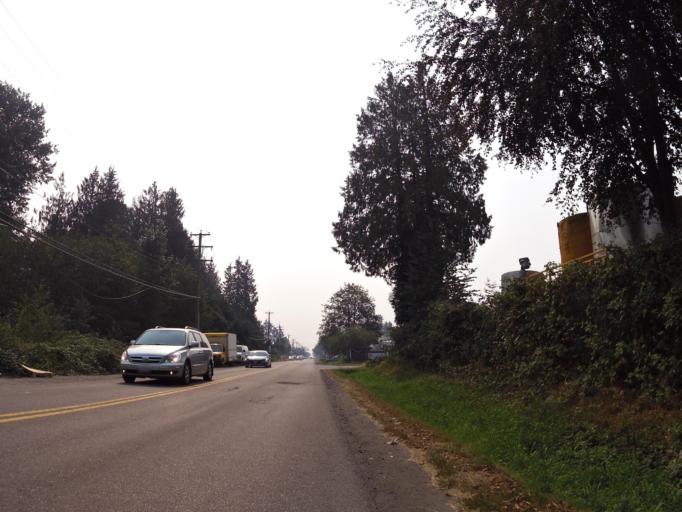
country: CA
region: British Columbia
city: Delta
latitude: 49.1551
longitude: -122.8791
